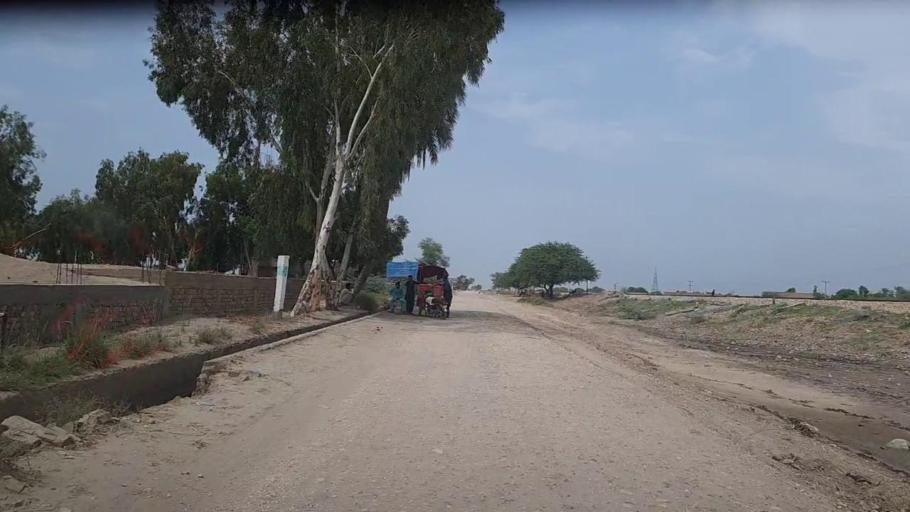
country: PK
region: Sindh
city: Bhiria
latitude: 26.8986
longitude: 68.2877
